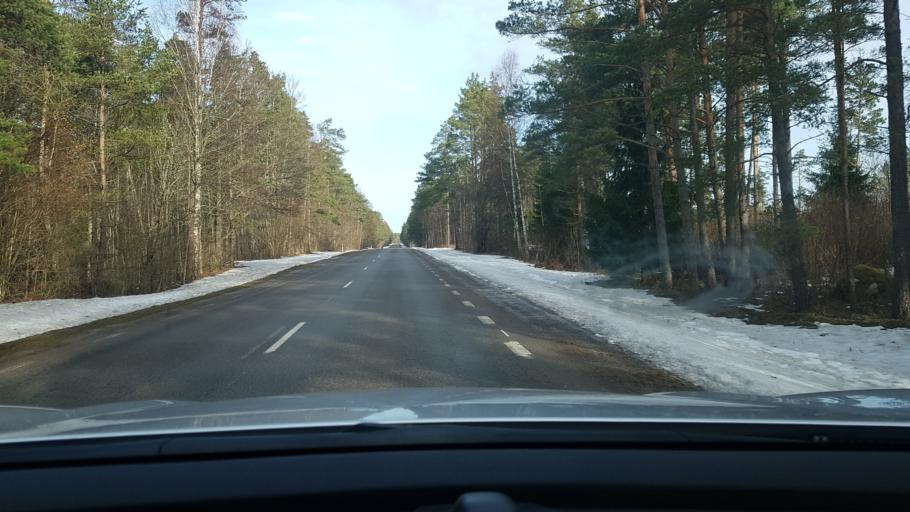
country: EE
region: Saare
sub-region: Kuressaare linn
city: Kuressaare
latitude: 58.4686
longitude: 22.7023
